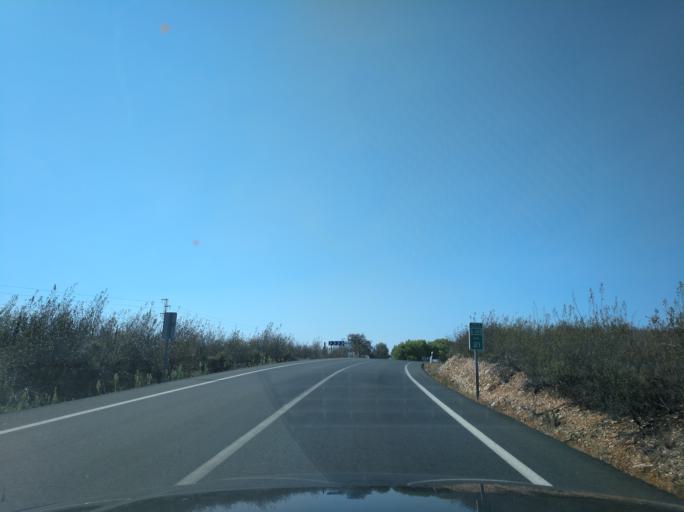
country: ES
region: Andalusia
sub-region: Provincia de Huelva
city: San Bartolome de la Torre
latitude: 37.4858
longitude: -7.1313
